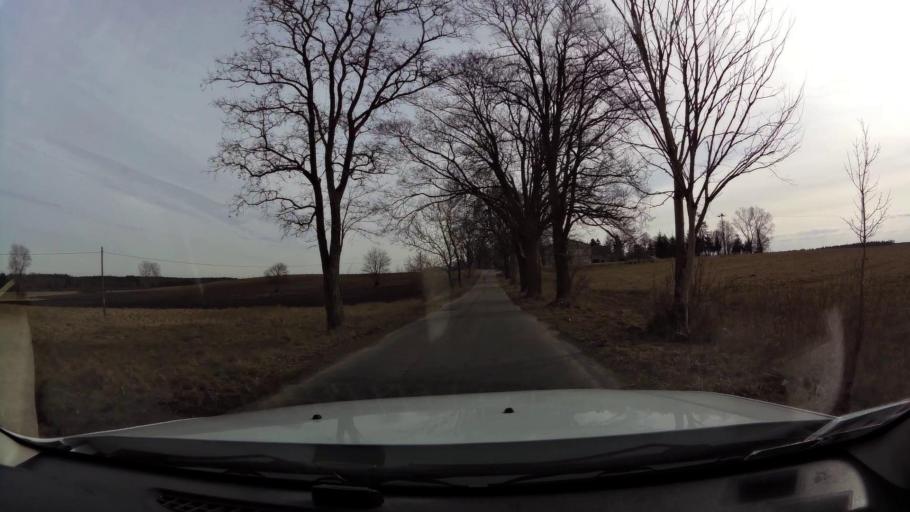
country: PL
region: West Pomeranian Voivodeship
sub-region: Powiat stargardzki
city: Insko
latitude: 53.4555
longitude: 15.6151
